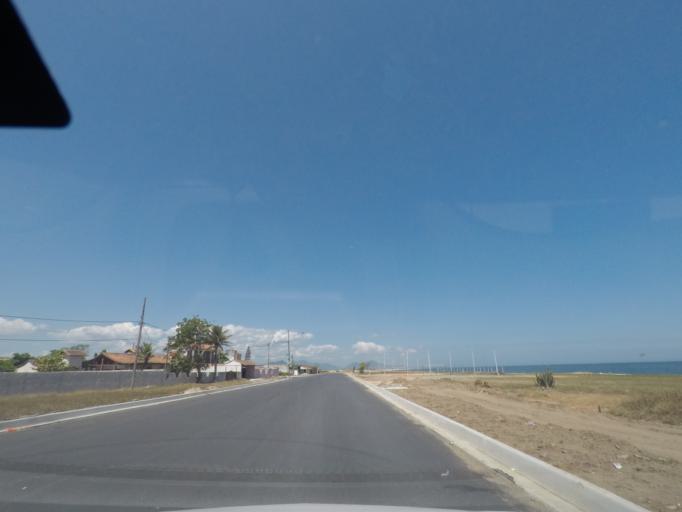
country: BR
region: Rio de Janeiro
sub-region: Marica
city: Marica
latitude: -22.9717
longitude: -42.9054
